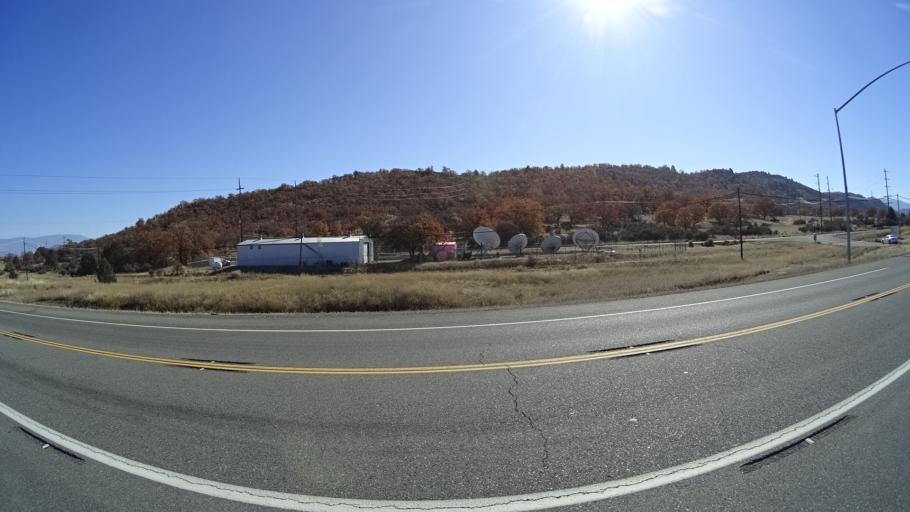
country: US
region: California
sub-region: Siskiyou County
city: Yreka
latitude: 41.7397
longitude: -122.6142
